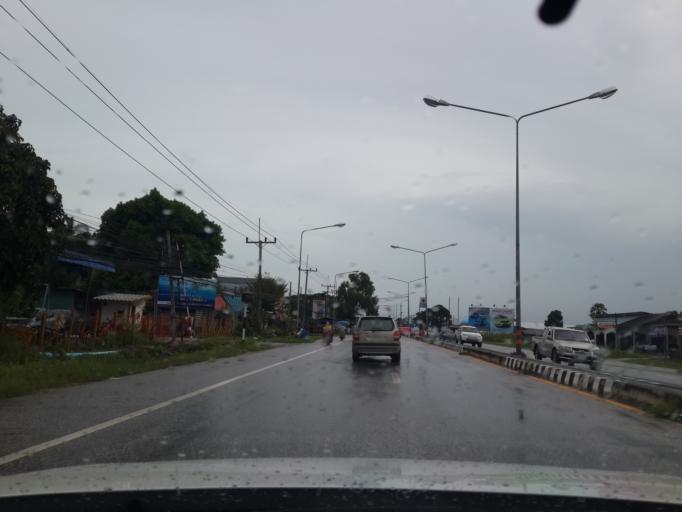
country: TH
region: Pattani
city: Pattani
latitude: 6.8568
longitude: 101.2229
